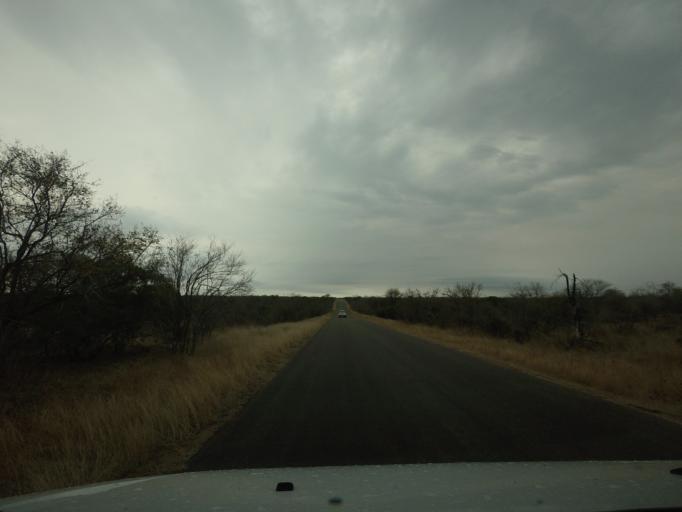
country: ZA
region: Limpopo
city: Thulamahashi
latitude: -24.4686
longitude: 31.4419
